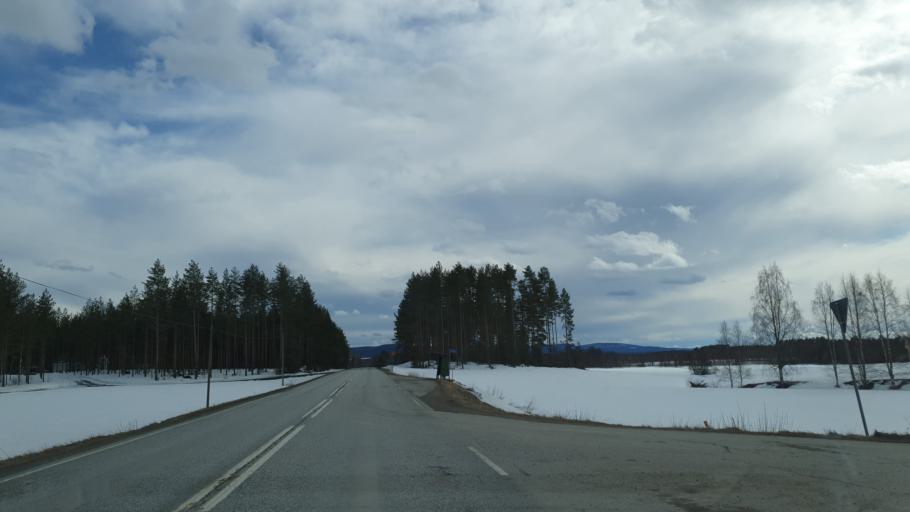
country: FI
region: Kainuu
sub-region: Kajaani
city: Vuokatti
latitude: 64.1825
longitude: 28.1893
